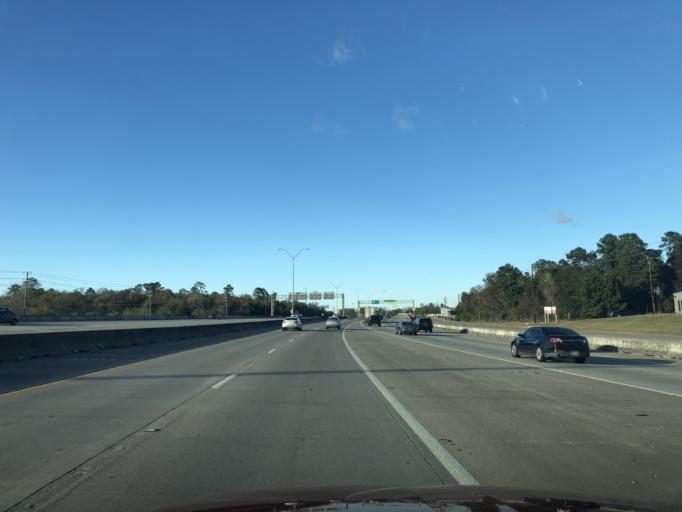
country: US
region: Texas
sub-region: Harris County
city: Cloverleaf
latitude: 29.7783
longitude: -95.1580
